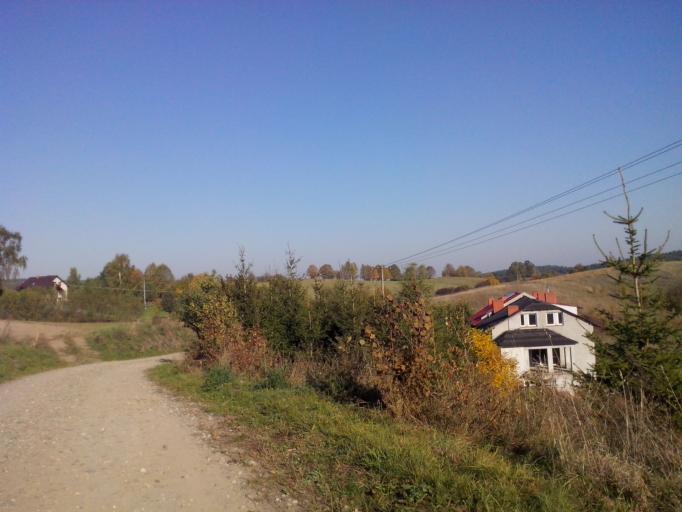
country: PL
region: Kujawsko-Pomorskie
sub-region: Powiat brodnicki
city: Gorzno
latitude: 53.2080
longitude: 19.6617
